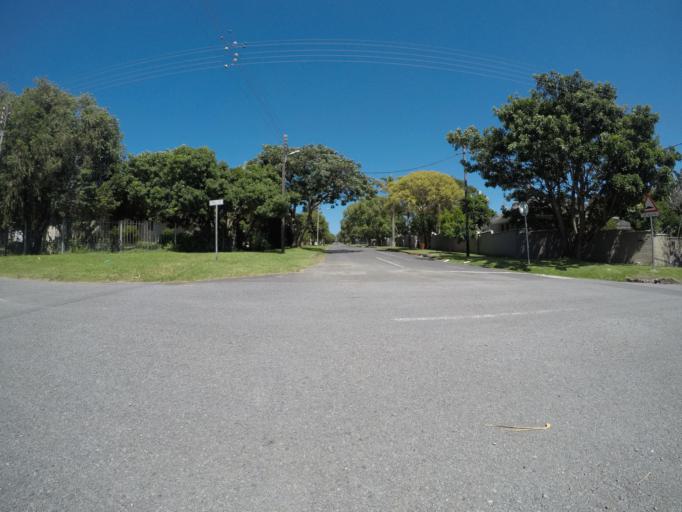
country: ZA
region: Eastern Cape
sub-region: Buffalo City Metropolitan Municipality
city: East London
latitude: -32.9716
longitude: 27.9427
